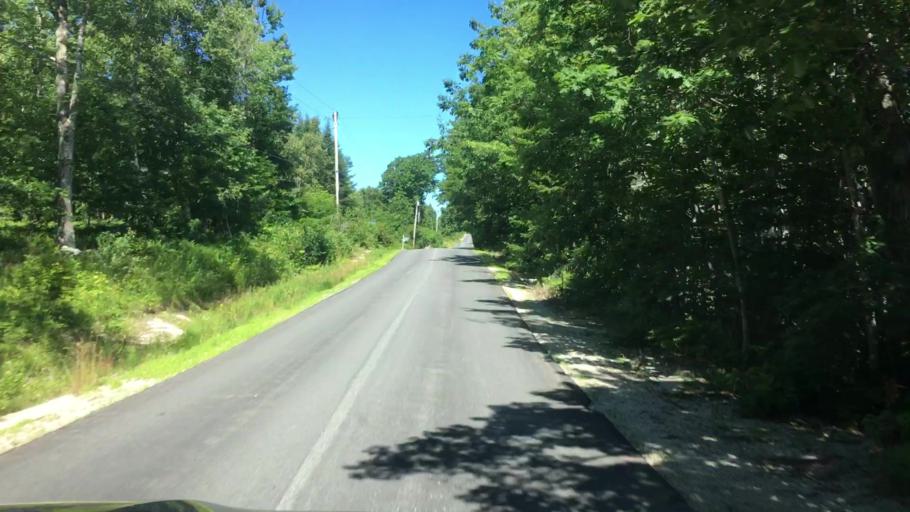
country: US
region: Maine
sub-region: Hancock County
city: Sedgwick
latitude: 44.3201
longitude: -68.6290
